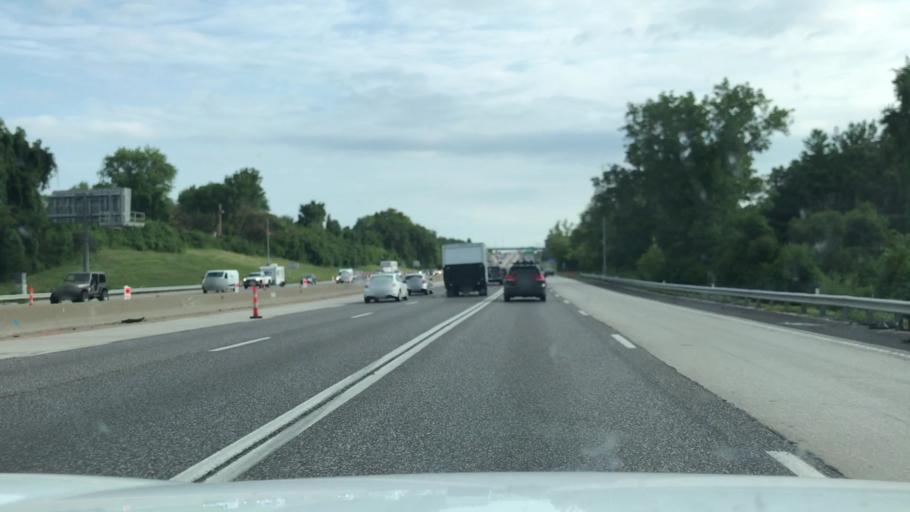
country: US
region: Missouri
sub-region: Saint Louis County
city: Maryland Heights
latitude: 38.7306
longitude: -90.4436
